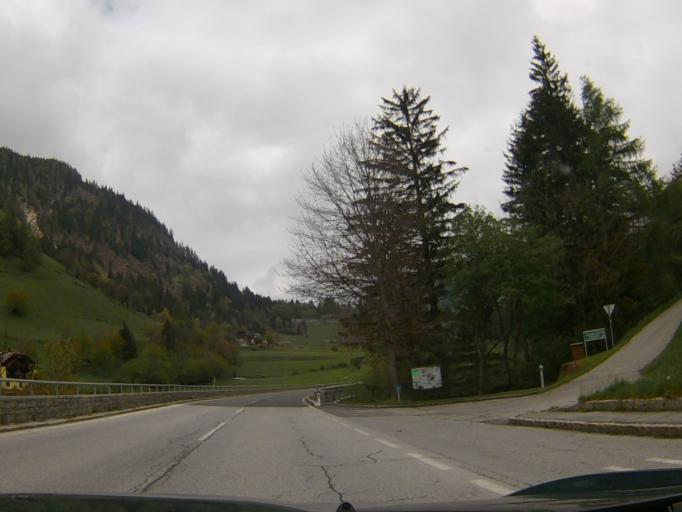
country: AT
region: Carinthia
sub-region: Politischer Bezirk Spittal an der Drau
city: Obervellach
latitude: 46.9584
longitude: 13.1844
